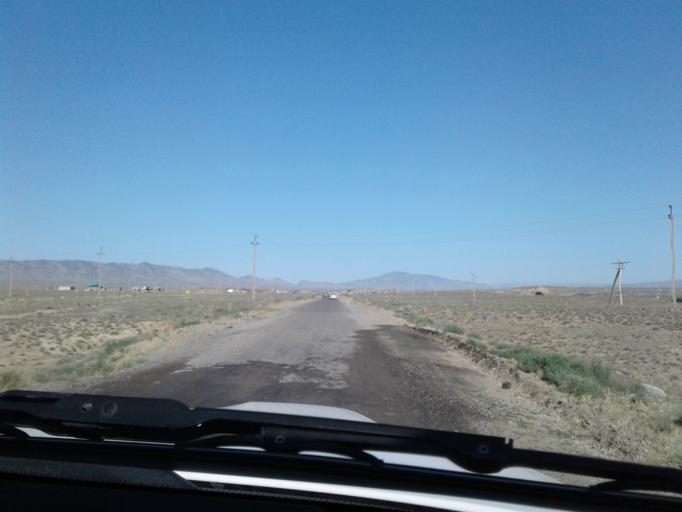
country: TM
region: Balkan
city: Magtymguly
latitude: 38.6855
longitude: 56.4413
